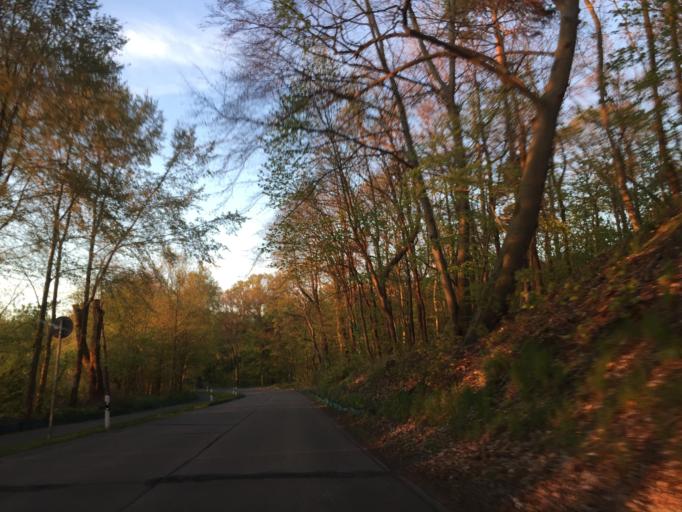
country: DE
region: Brandenburg
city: Potsdam
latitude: 52.3747
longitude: 13.0380
